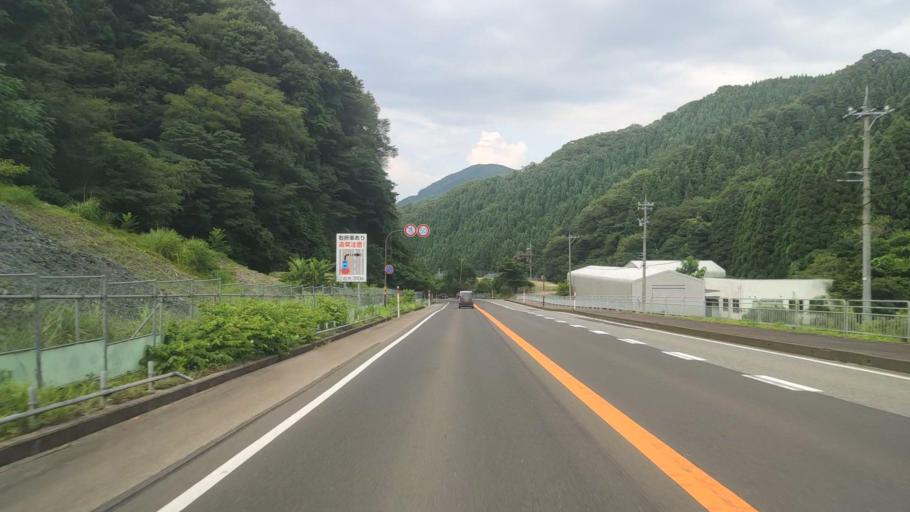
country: JP
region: Fukui
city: Takefu
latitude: 35.8115
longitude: 136.0981
